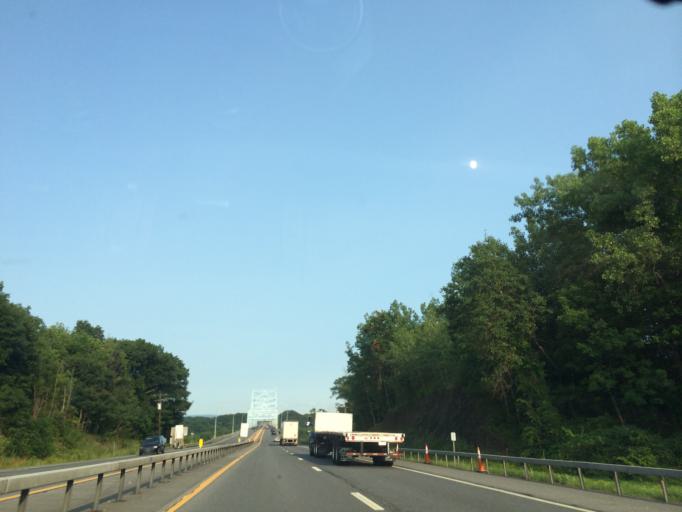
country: US
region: New York
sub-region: Rensselaer County
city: Castleton-on-Hudson
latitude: 42.5120
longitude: -73.7821
